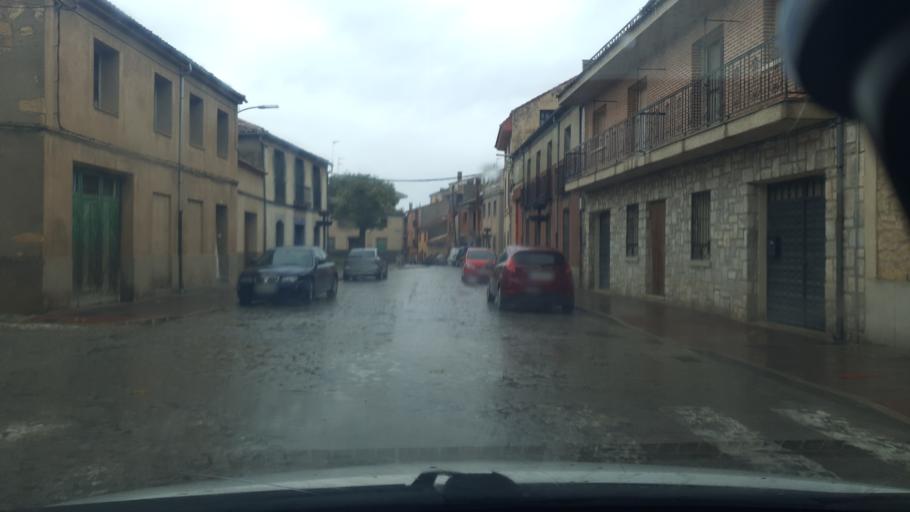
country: ES
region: Castille and Leon
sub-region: Provincia de Segovia
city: Carbonero el Mayor
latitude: 41.1206
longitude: -4.2648
